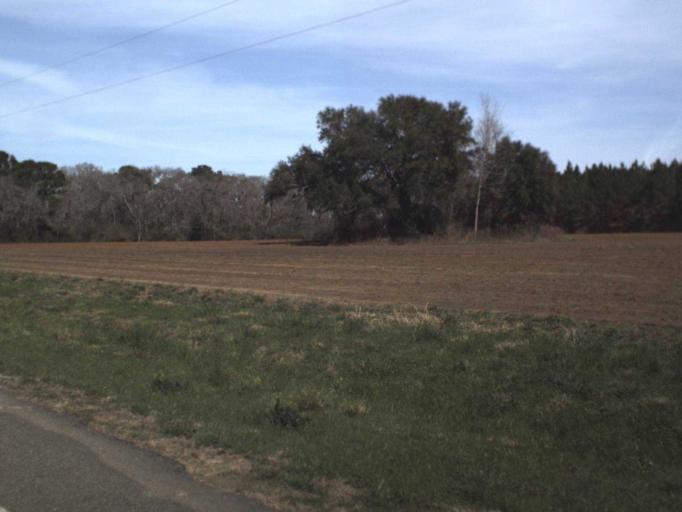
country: US
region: Florida
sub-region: Washington County
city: Chipley
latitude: 30.8313
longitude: -85.5330
